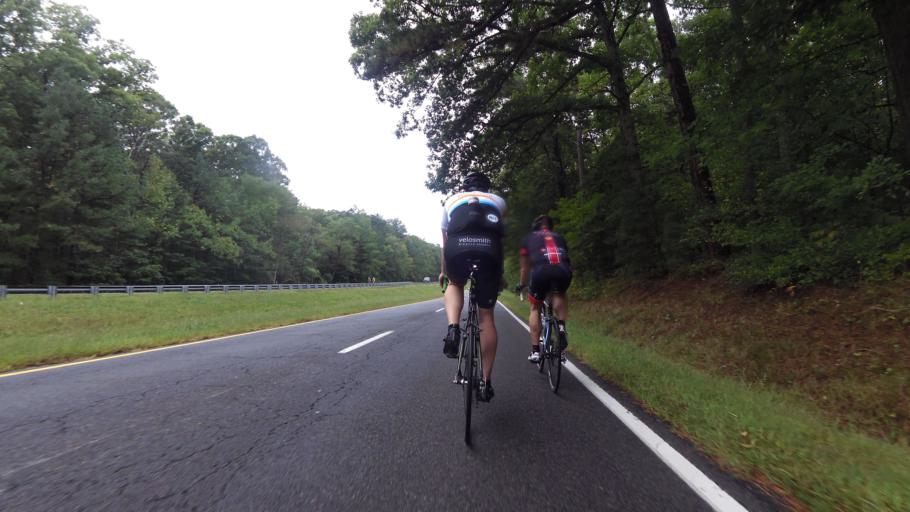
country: US
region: Virginia
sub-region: Henrico County
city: Short Pump
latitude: 37.6012
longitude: -77.6911
